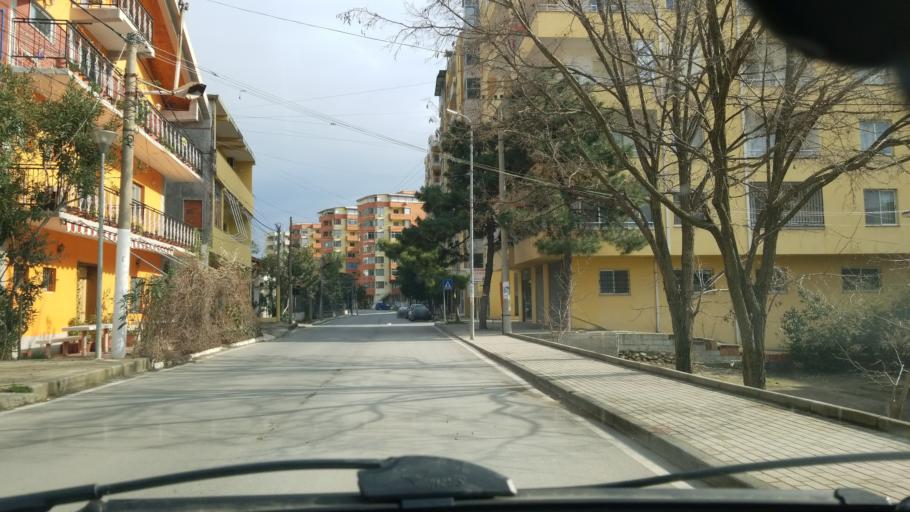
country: AL
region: Lezhe
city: Shengjin
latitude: 41.8108
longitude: 19.5975
